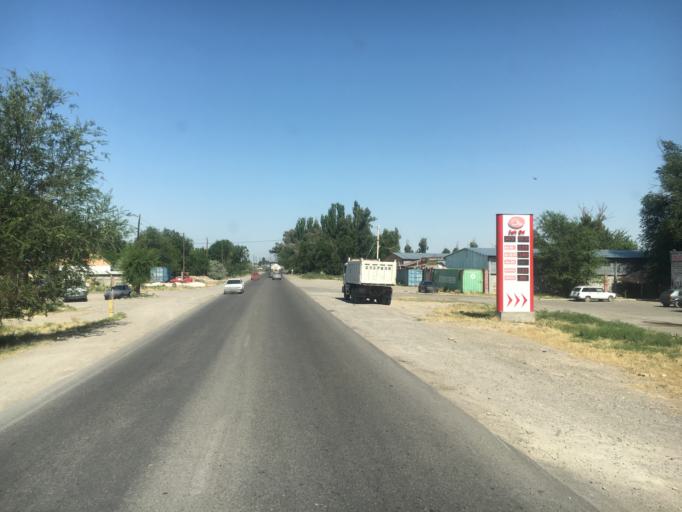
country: KZ
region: Zhambyl
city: Taraz
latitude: 42.9430
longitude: 71.4129
